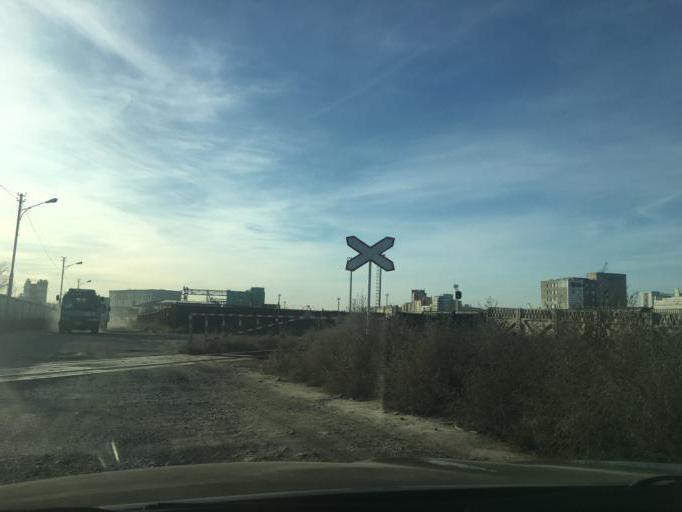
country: MN
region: Ulaanbaatar
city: Ulaanbaatar
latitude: 47.9071
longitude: 106.8860
